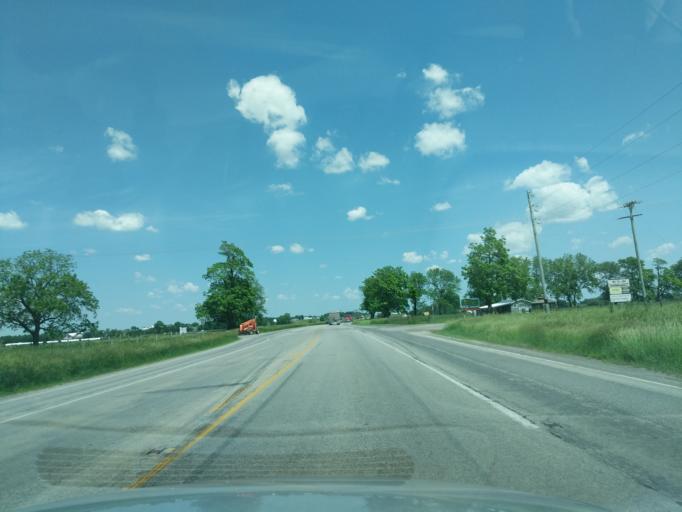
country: US
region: Indiana
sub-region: LaGrange County
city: Topeka
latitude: 41.6106
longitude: -85.5792
